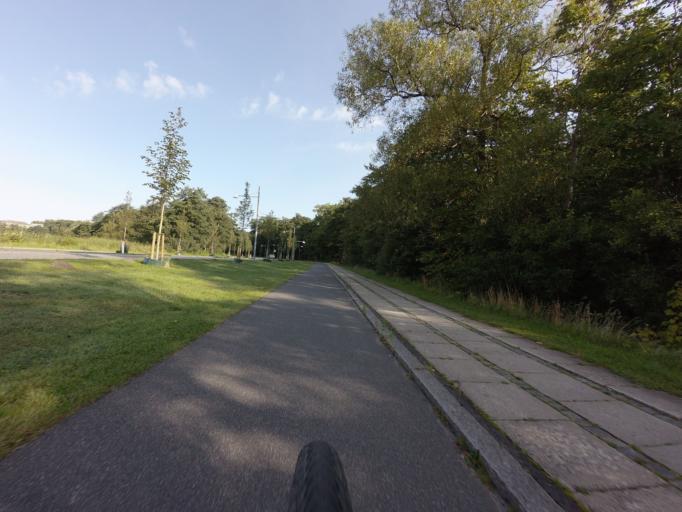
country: DK
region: Zealand
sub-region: Soro Kommune
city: Soro
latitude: 55.4271
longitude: 11.5652
